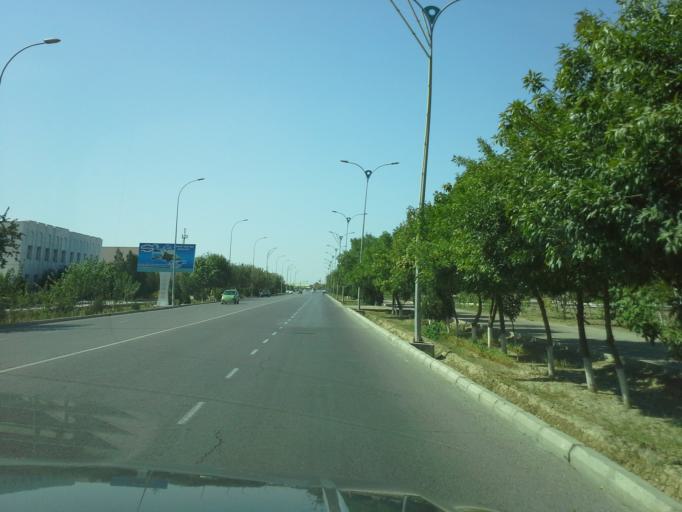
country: TM
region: Dasoguz
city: Dasoguz
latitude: 41.8435
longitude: 59.9362
